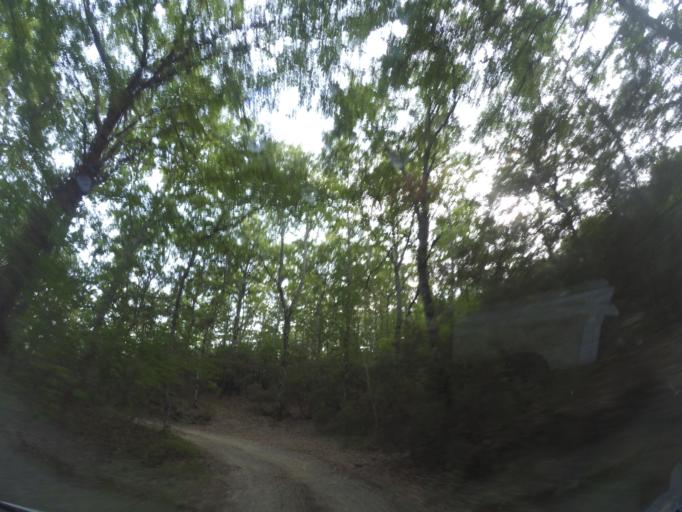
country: IT
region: Tuscany
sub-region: Province of Arezzo
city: Castiglion Fibocchi
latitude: 43.5527
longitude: 11.7881
